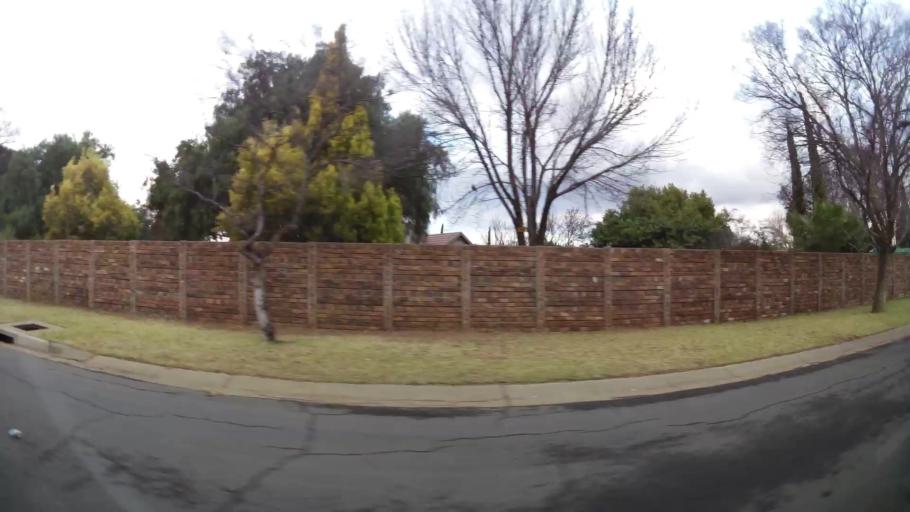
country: ZA
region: Orange Free State
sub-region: Lejweleputswa District Municipality
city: Welkom
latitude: -27.9560
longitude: 26.7384
